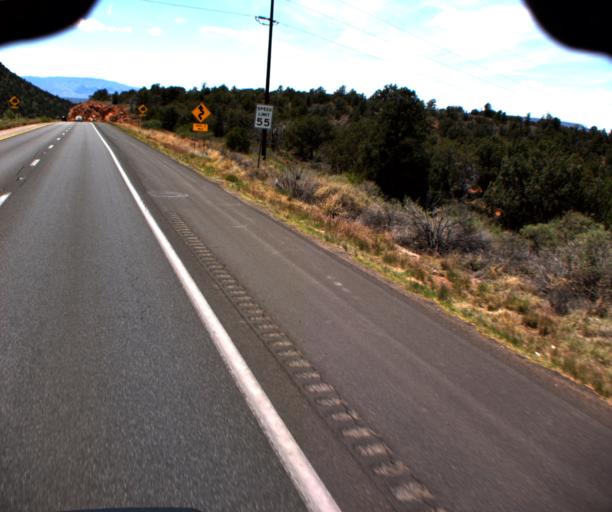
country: US
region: Arizona
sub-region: Yavapai County
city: West Sedona
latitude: 34.8482
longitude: -111.8346
